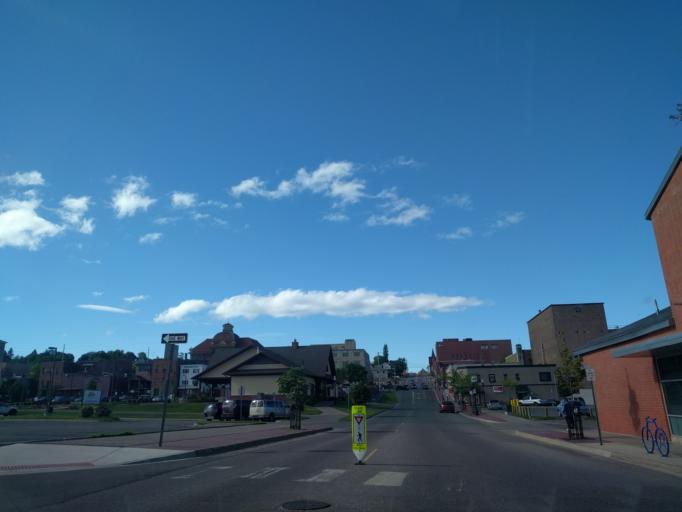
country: US
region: Michigan
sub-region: Marquette County
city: Marquette
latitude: 46.5420
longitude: -87.3959
